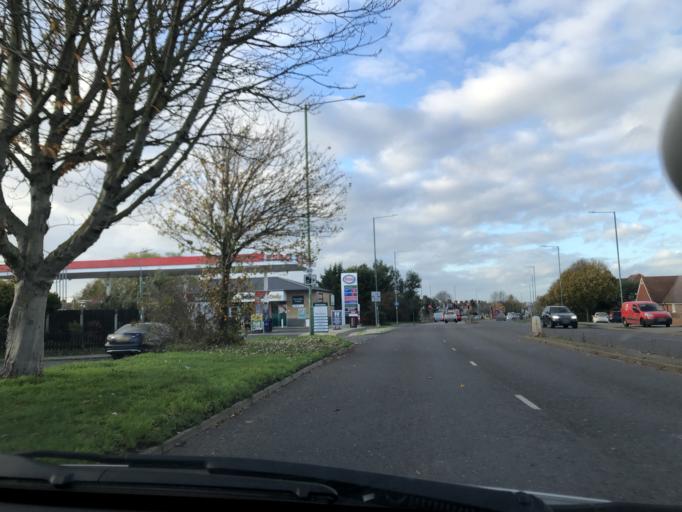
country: GB
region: England
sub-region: Kent
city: Dartford
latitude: 51.4403
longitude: 0.1974
